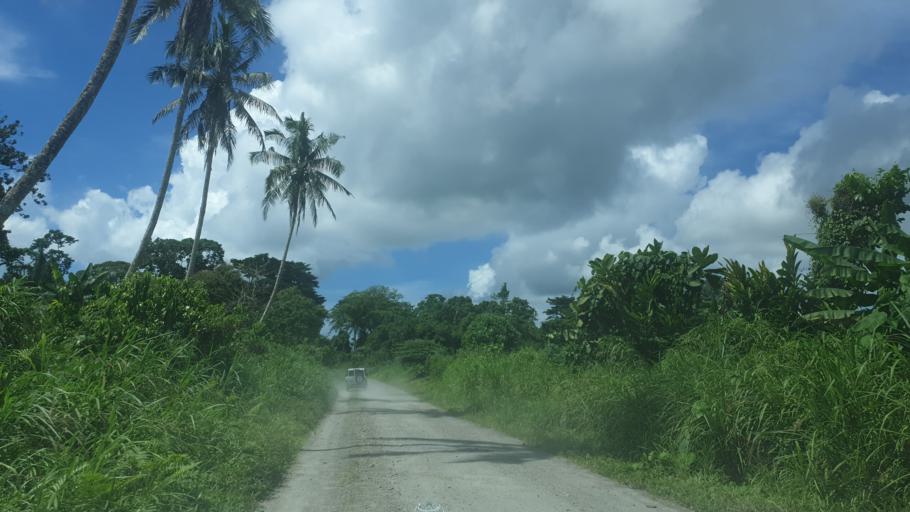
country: PG
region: Bougainville
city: Panguna
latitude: -6.7347
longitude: 155.4953
